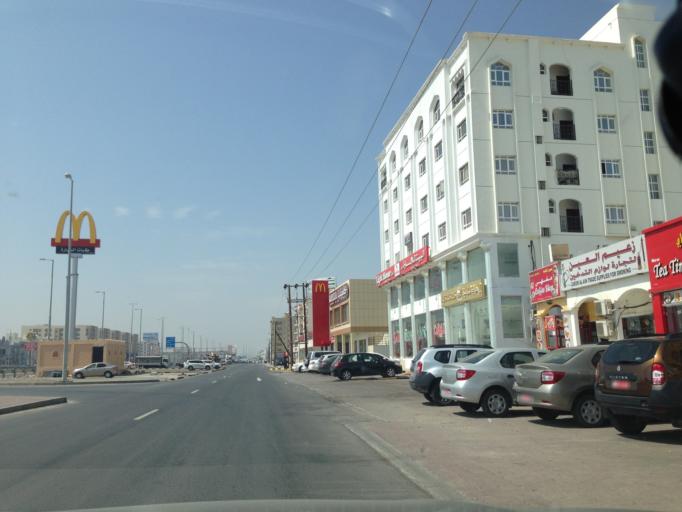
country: OM
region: Al Batinah
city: Barka'
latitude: 23.6648
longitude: 57.8983
